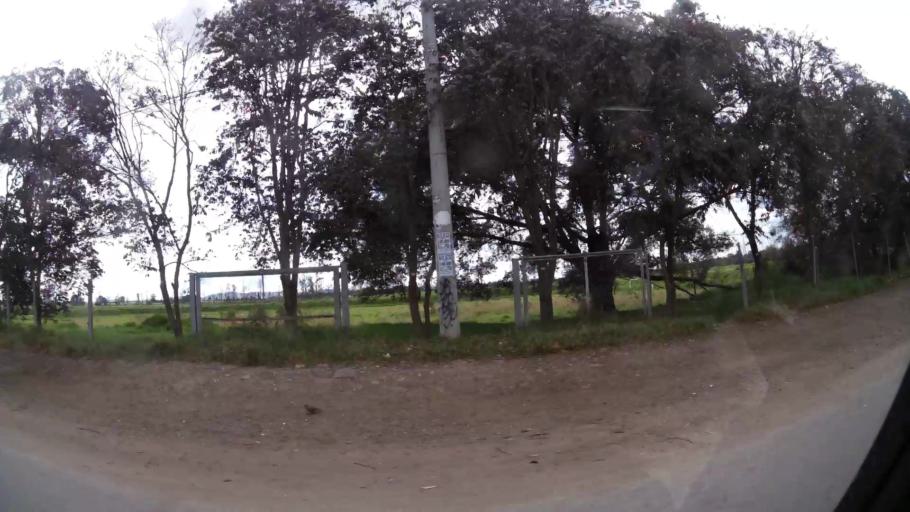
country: CO
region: Cundinamarca
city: Funza
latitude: 4.7205
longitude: -74.1435
